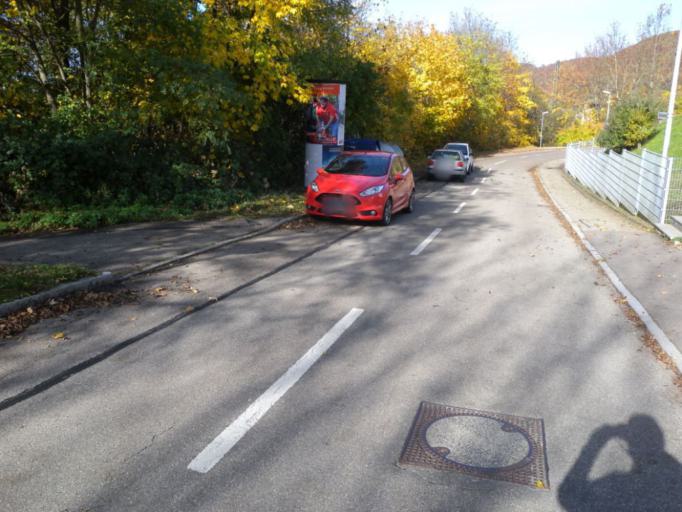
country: DE
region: Baden-Wuerttemberg
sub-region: Regierungsbezirk Stuttgart
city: Geislingen an der Steige
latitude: 48.6199
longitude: 9.8426
